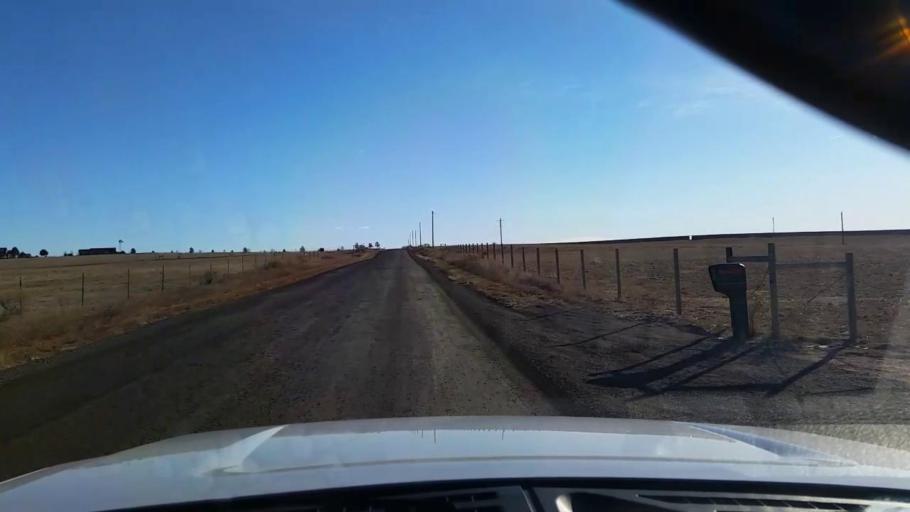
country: US
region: Colorado
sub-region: Larimer County
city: Wellington
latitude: 40.7696
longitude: -105.1128
